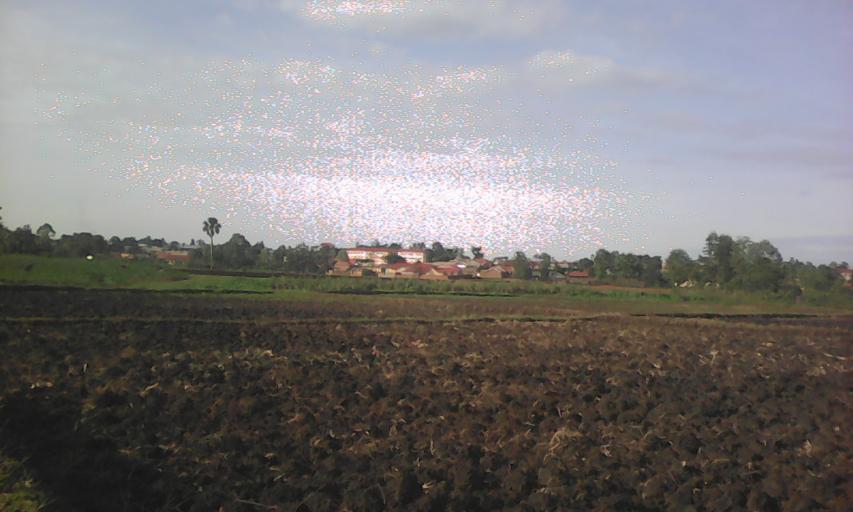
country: UG
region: Eastern Region
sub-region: Mbale District
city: Mbale
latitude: 1.0879
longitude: 34.1661
